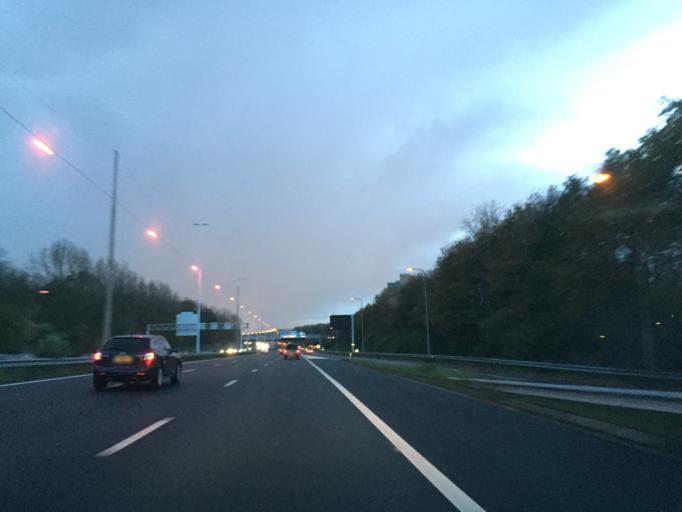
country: NL
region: South Holland
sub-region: Gemeente Rijswijk
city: Rijswijk
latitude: 52.0360
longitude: 4.3356
